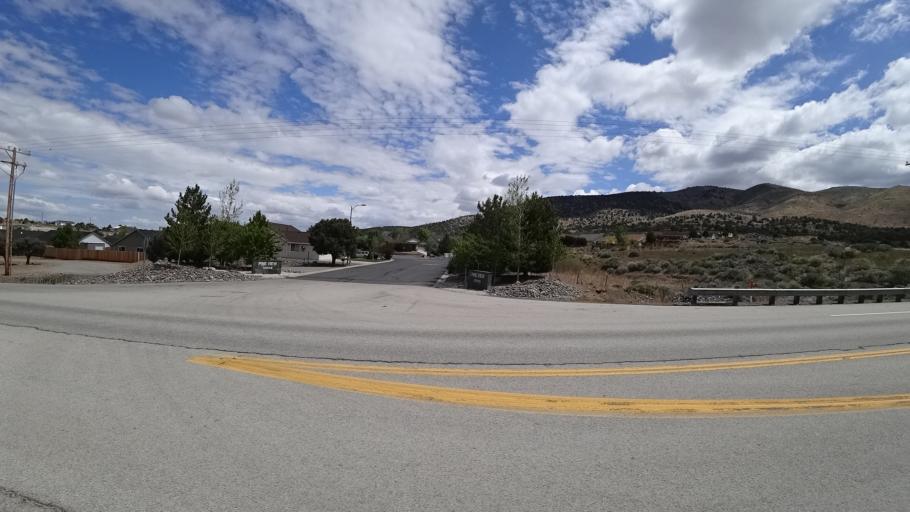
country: US
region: Nevada
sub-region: Douglas County
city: Gardnerville Ranchos
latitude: 38.8490
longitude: -119.6464
